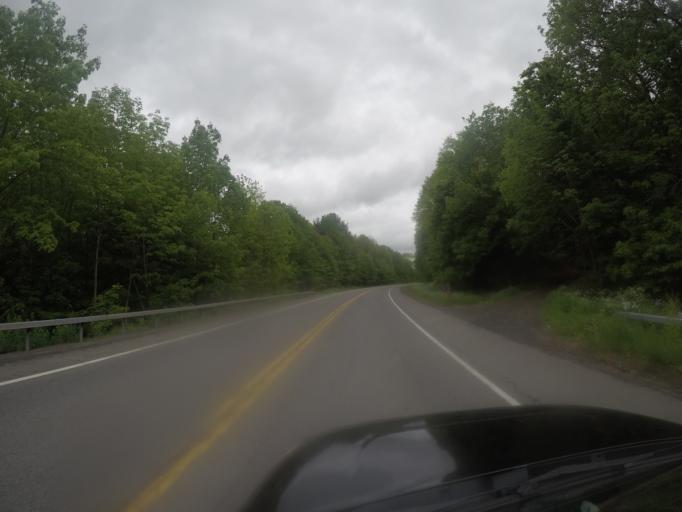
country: US
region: New York
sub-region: Ulster County
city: Shokan
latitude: 42.0859
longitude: -74.3316
